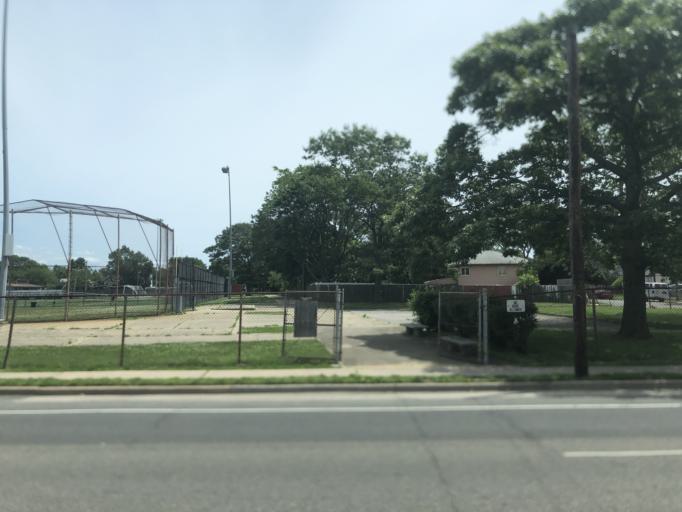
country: US
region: New York
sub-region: Nassau County
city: Hempstead
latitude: 40.6956
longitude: -73.6219
